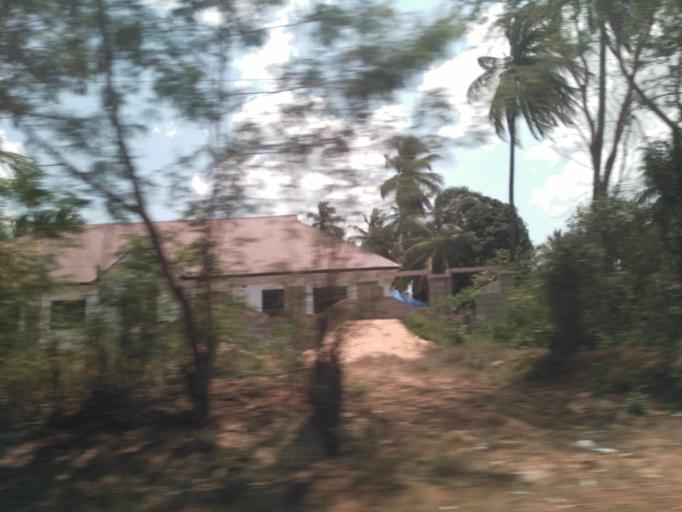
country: TZ
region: Dar es Salaam
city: Dar es Salaam
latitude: -6.8410
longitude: 39.3510
